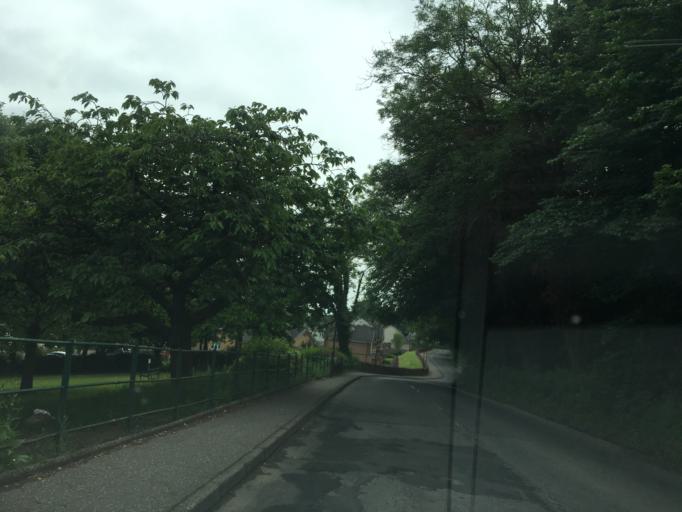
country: GB
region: Scotland
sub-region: Stirling
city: Stirling
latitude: 56.1081
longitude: -3.9651
